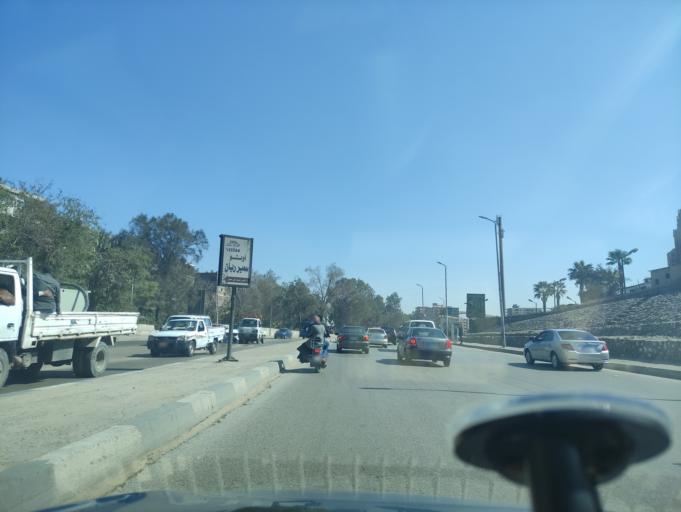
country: EG
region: Muhafazat al Qahirah
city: Cairo
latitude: 30.0545
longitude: 31.2917
